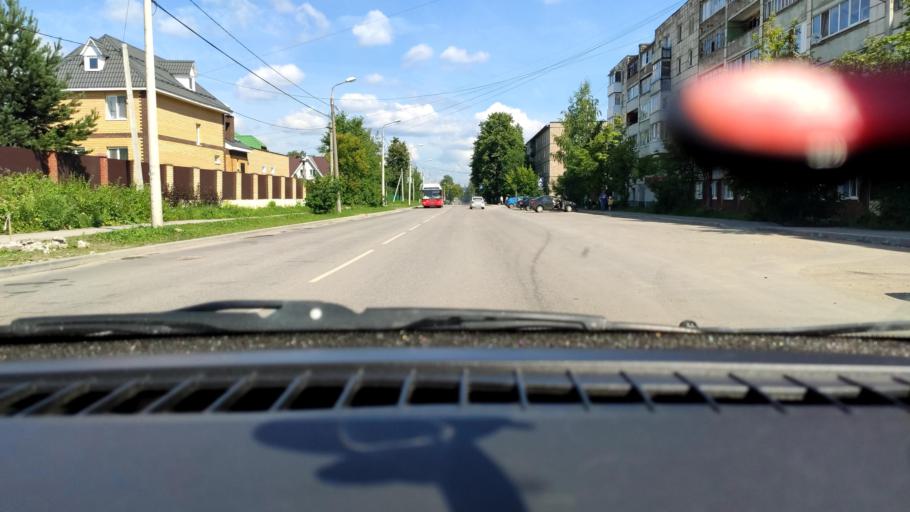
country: RU
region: Perm
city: Perm
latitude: 58.1047
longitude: 56.2969
